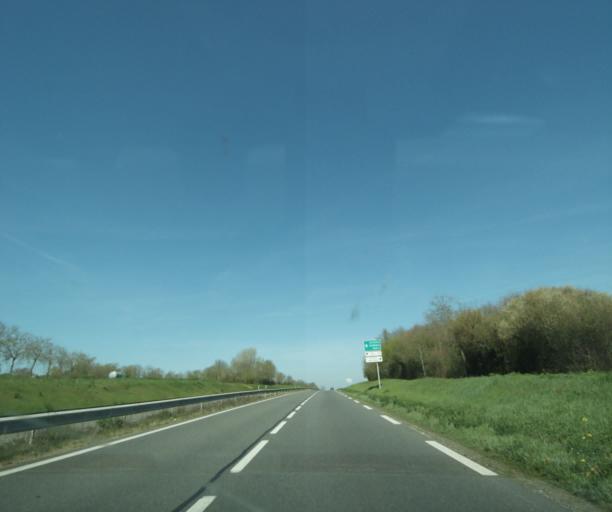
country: FR
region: Bourgogne
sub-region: Departement de la Nievre
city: Saint-Pierre-le-Moutier
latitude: 46.7807
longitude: 3.1290
